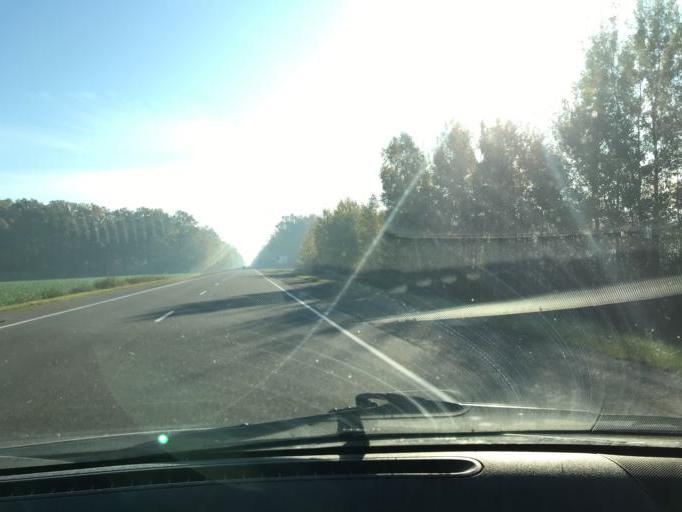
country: BY
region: Brest
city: Horad Luninyets
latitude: 52.3107
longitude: 26.6694
